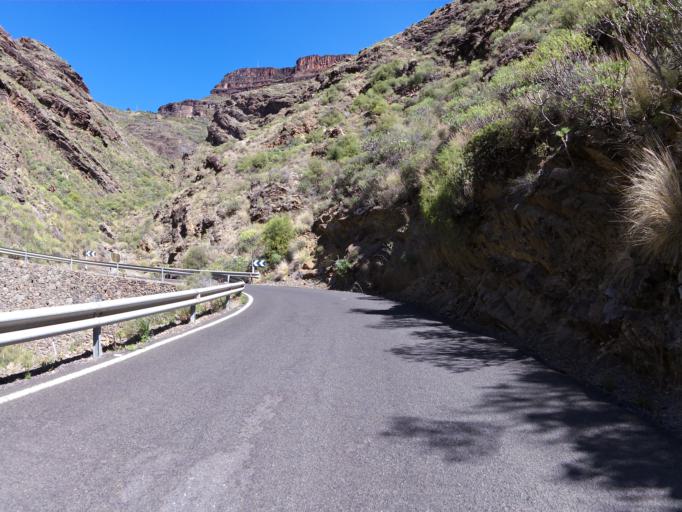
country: ES
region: Canary Islands
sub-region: Provincia de Las Palmas
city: Artenara
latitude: 27.9958
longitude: -15.6879
